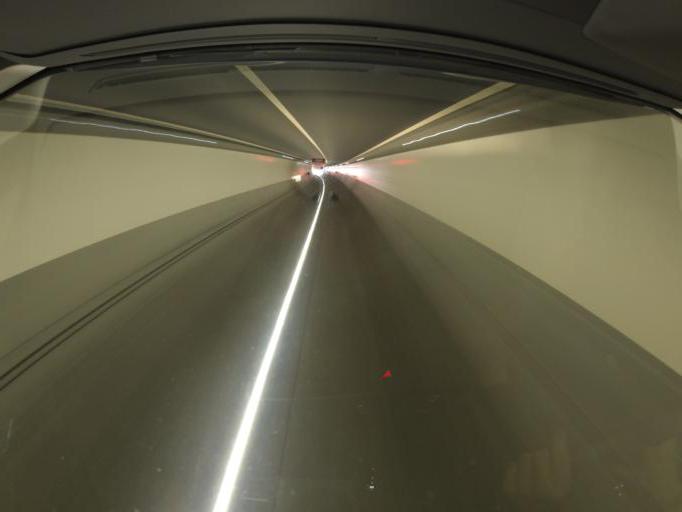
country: CH
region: Saint Gallen
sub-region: Wahlkreis See-Gaster
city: Schmerikon
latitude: 47.2317
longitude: 8.9579
